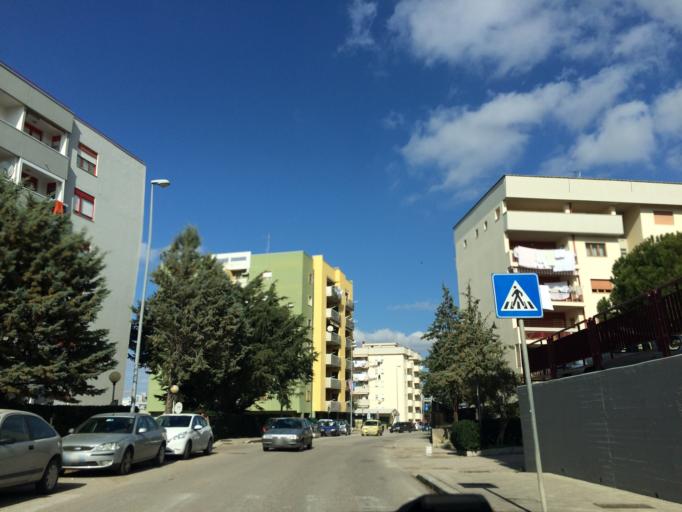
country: IT
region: Basilicate
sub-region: Provincia di Matera
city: Matera
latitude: 40.6700
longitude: 16.5864
